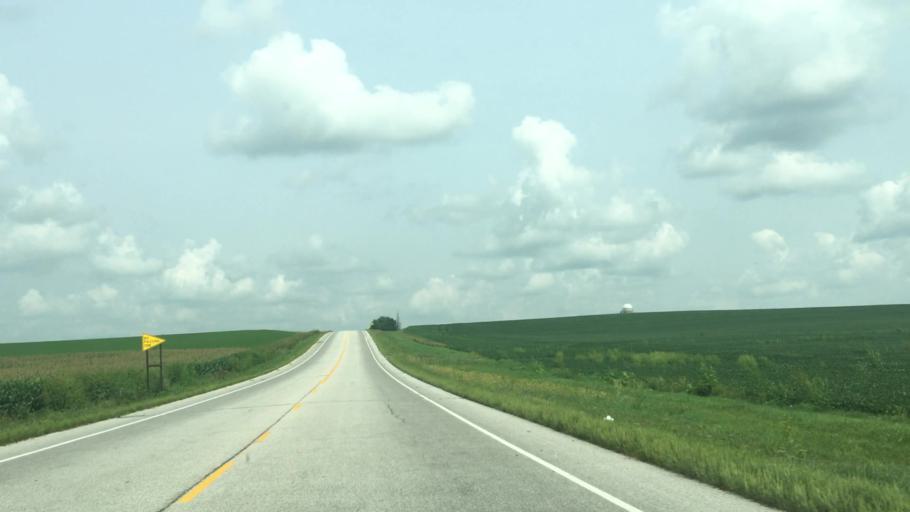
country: US
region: Minnesota
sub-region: Fillmore County
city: Harmony
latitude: 43.5969
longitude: -91.9297
